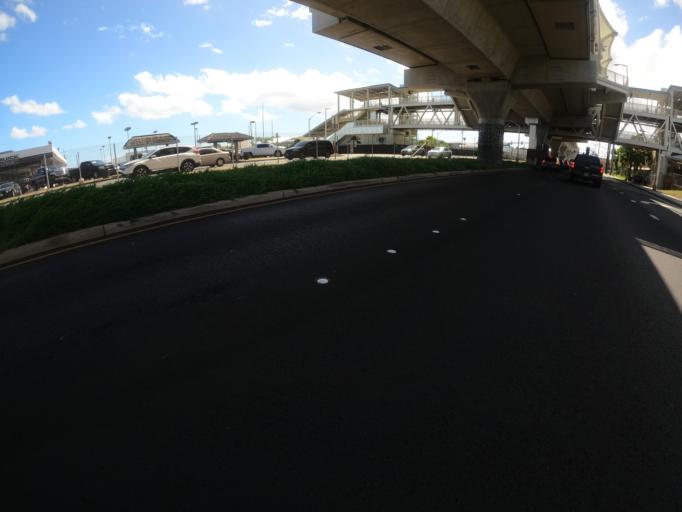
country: US
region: Hawaii
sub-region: Honolulu County
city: Waipahu
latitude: 21.3785
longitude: -158.0223
